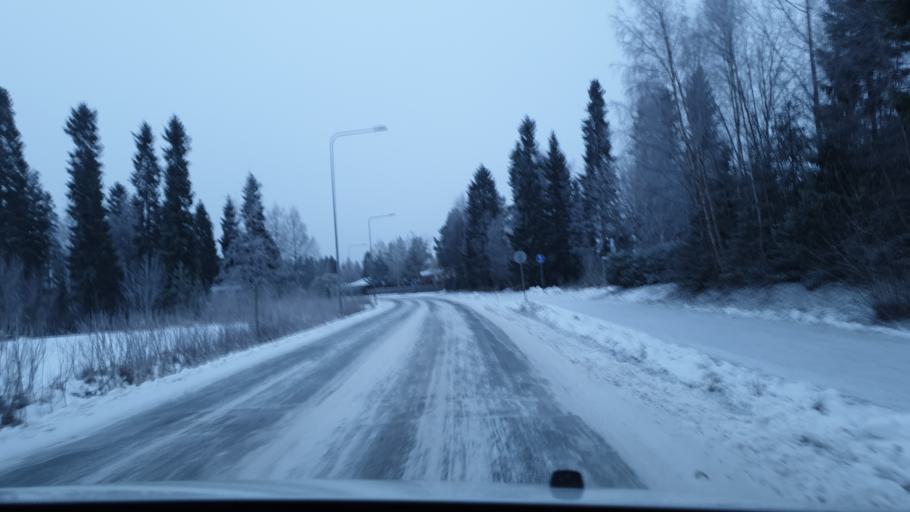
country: FI
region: Lapland
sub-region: Kemi-Tornio
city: Kemi
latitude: 65.7398
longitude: 24.6082
